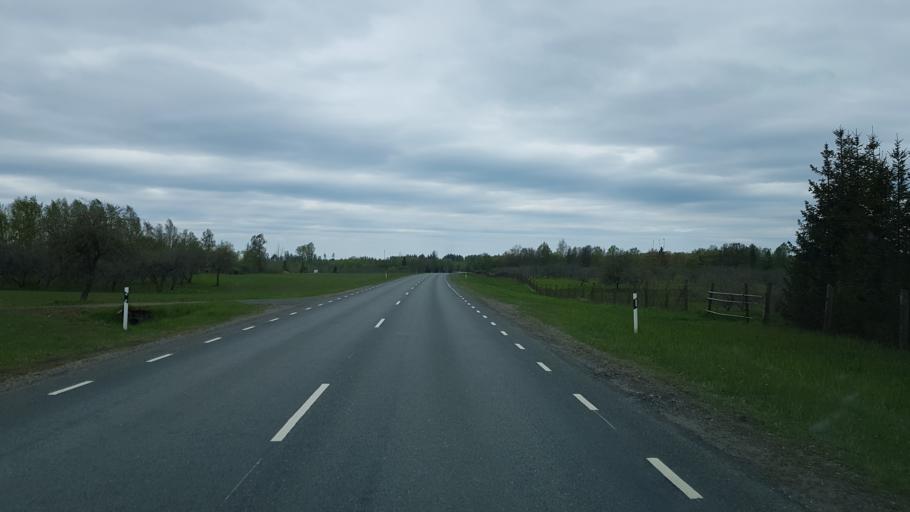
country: EE
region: Viljandimaa
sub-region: Suure-Jaani vald
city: Suure-Jaani
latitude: 58.5225
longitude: 25.5255
